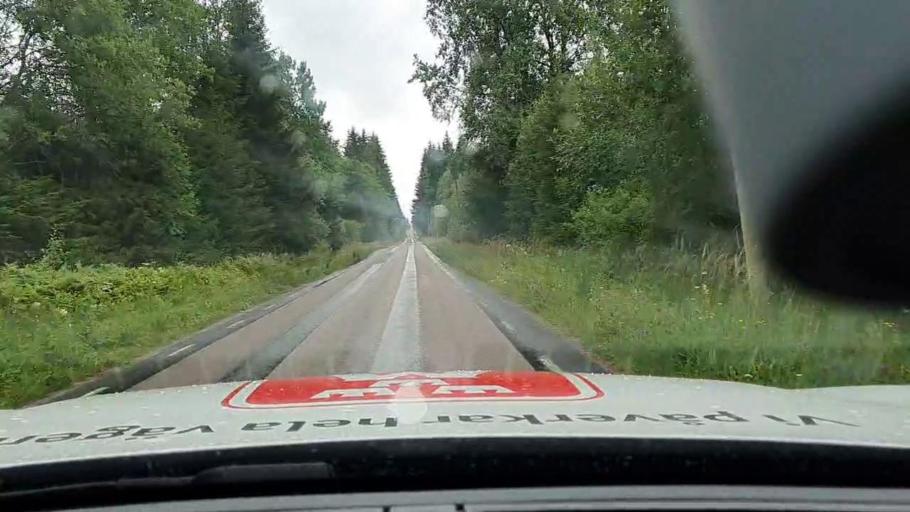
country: SE
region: Vaestra Goetaland
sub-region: Skovde Kommun
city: Skoevde
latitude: 58.4477
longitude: 13.7623
